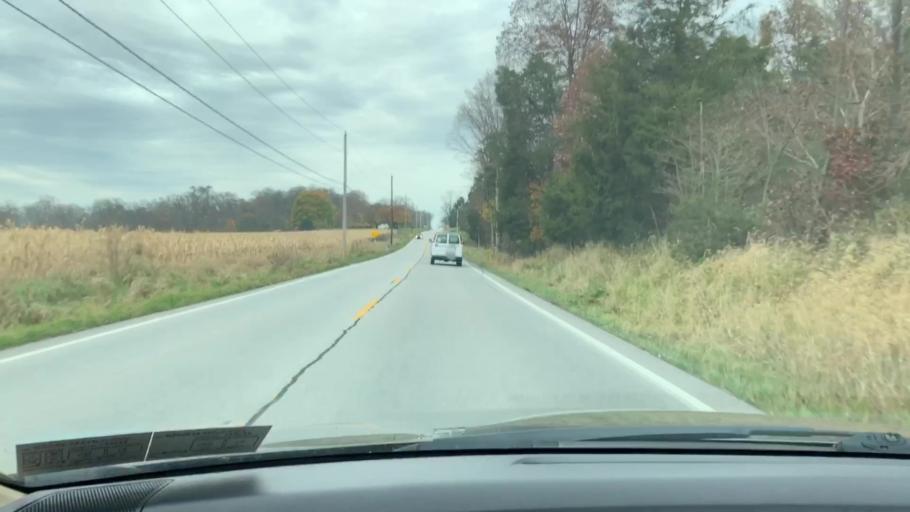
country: US
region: Pennsylvania
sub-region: Adams County
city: Lake Meade
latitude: 39.9456
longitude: -77.0892
